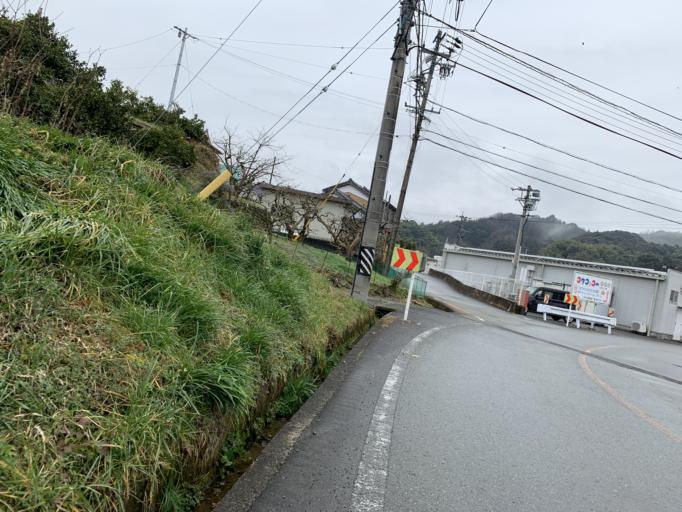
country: JP
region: Mie
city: Ise
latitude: 34.4779
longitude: 136.5423
